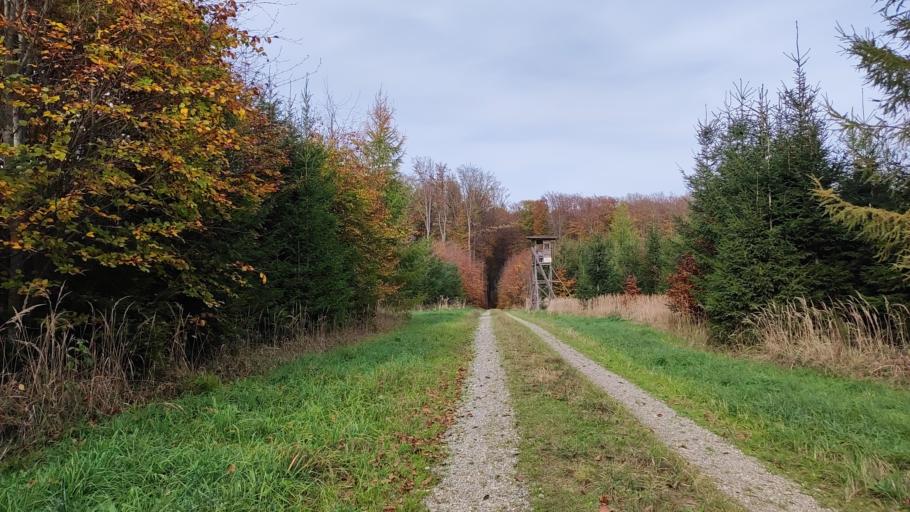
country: DE
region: Bavaria
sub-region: Swabia
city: Langenneufnach
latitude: 48.2699
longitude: 10.5698
